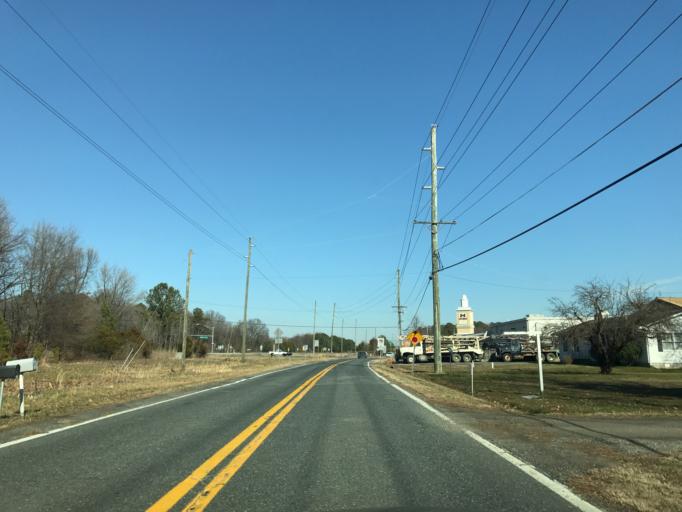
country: US
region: Maryland
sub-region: Queen Anne's County
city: Grasonville
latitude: 38.9833
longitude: -76.1624
